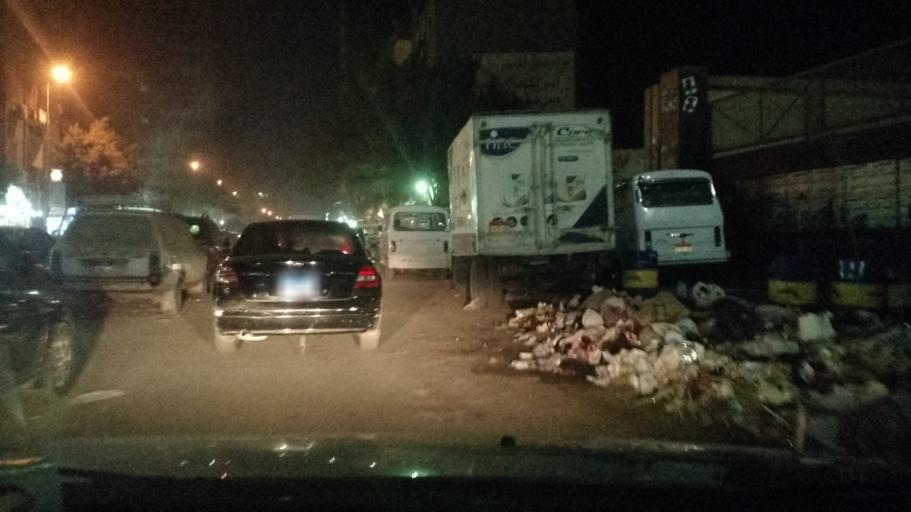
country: EG
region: Al Jizah
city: Al Jizah
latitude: 29.9983
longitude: 31.2000
